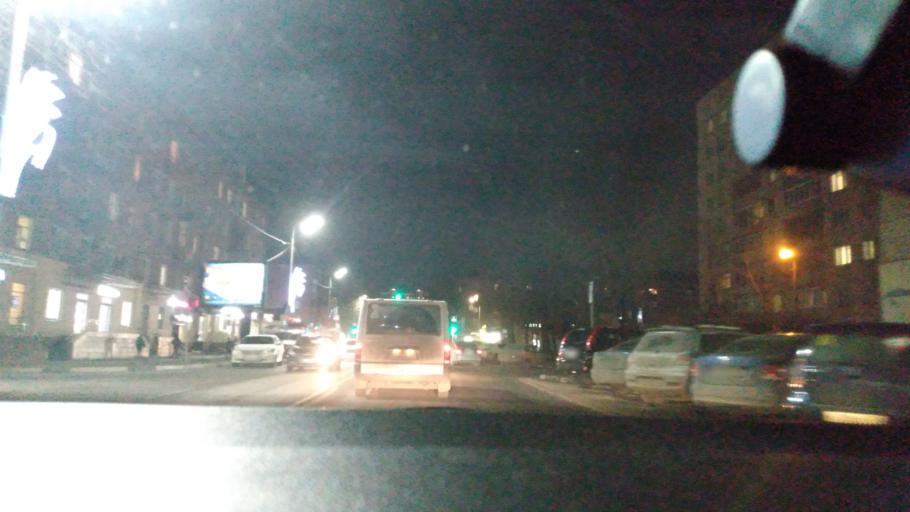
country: RU
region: Moskovskaya
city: Balashikha
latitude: 55.8008
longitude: 37.9346
